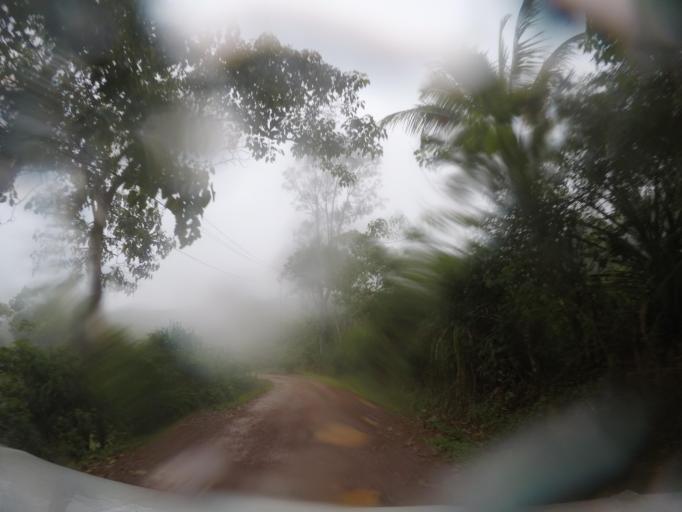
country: TL
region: Baucau
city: Venilale
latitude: -8.6383
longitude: 126.4175
